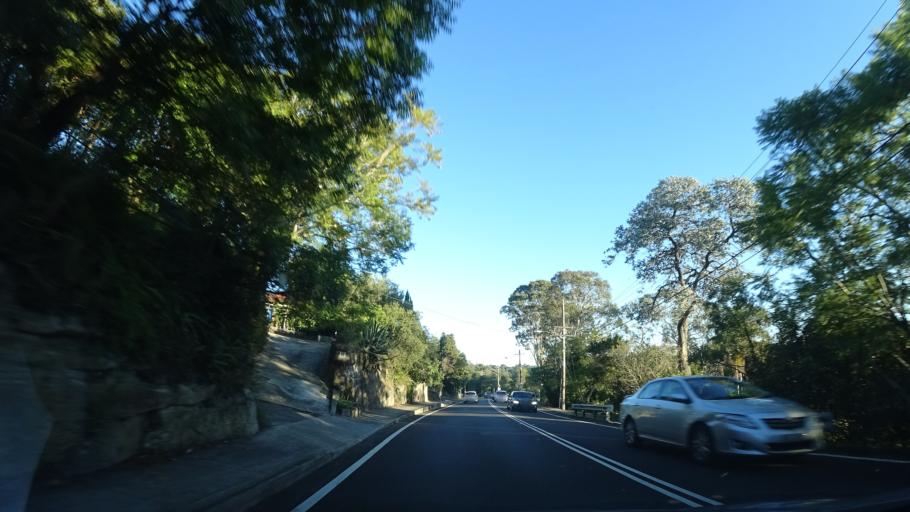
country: AU
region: New South Wales
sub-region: Willoughby
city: Chatswood West
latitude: -33.7951
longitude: 151.1669
